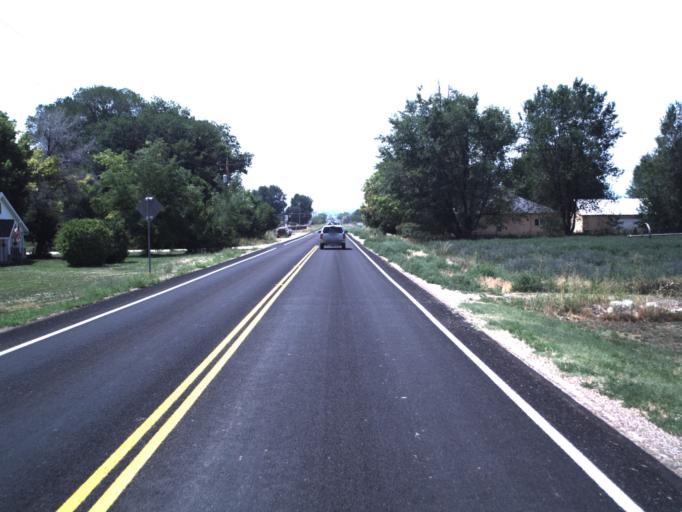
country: US
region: Utah
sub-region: Duchesne County
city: Roosevelt
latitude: 40.4038
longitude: -109.7970
